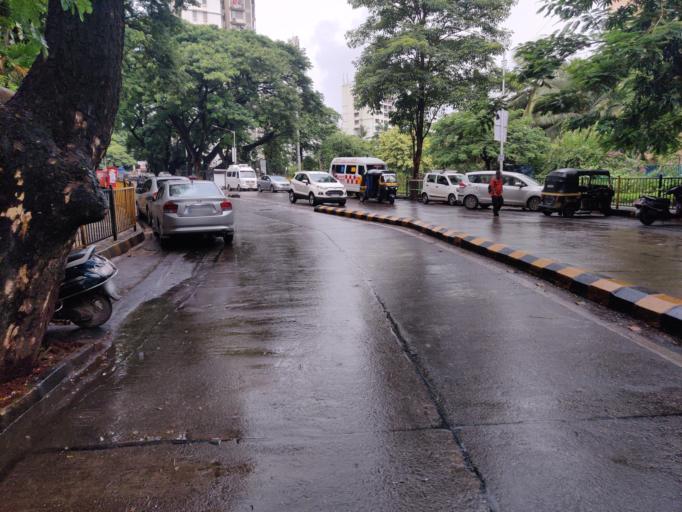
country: IN
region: Maharashtra
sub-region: Mumbai Suburban
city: Borivli
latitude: 19.2474
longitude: 72.8542
